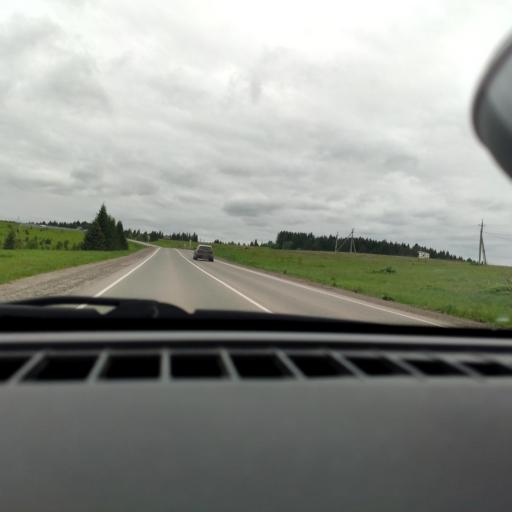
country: RU
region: Perm
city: Kultayevo
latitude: 57.8924
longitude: 55.7963
